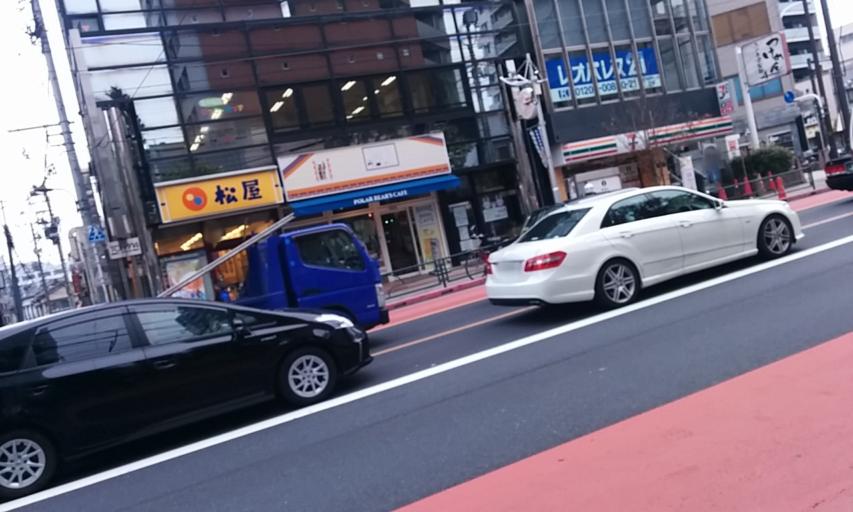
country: JP
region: Tokyo
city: Tokyo
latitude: 35.7115
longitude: 139.7094
